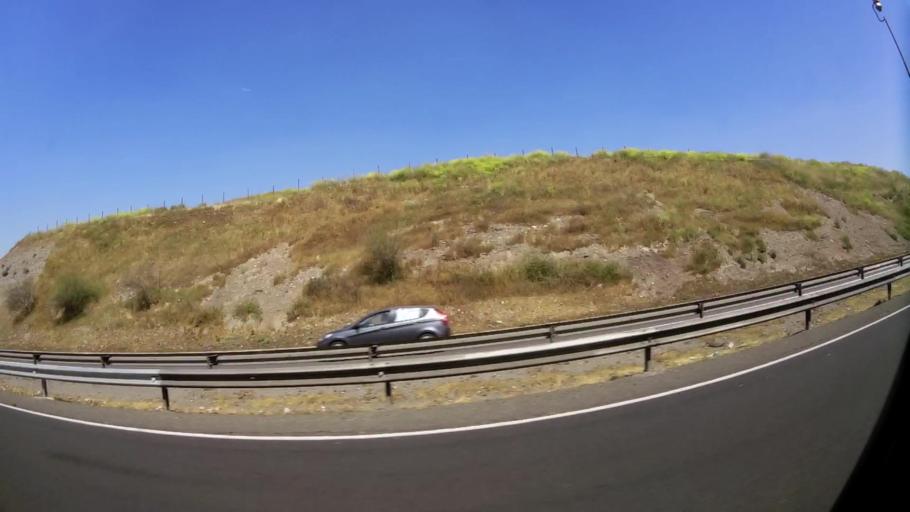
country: CL
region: Santiago Metropolitan
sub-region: Provincia de Santiago
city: Lo Prado
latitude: -33.4836
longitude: -70.7213
